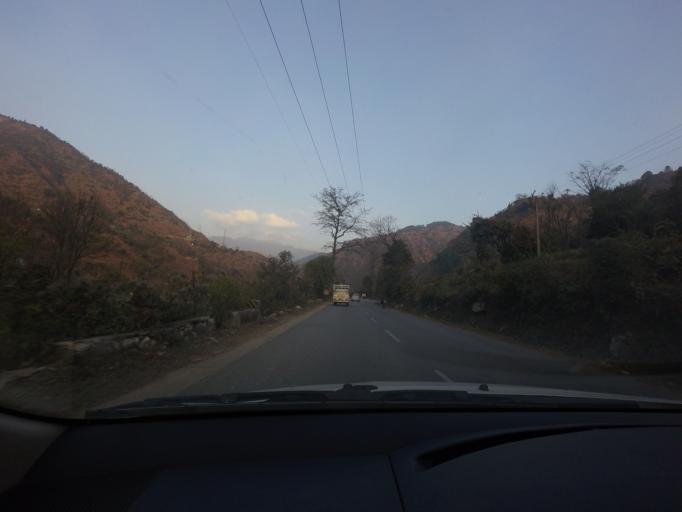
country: IN
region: Himachal Pradesh
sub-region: Mandi
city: Mandi
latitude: 31.7018
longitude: 76.9674
